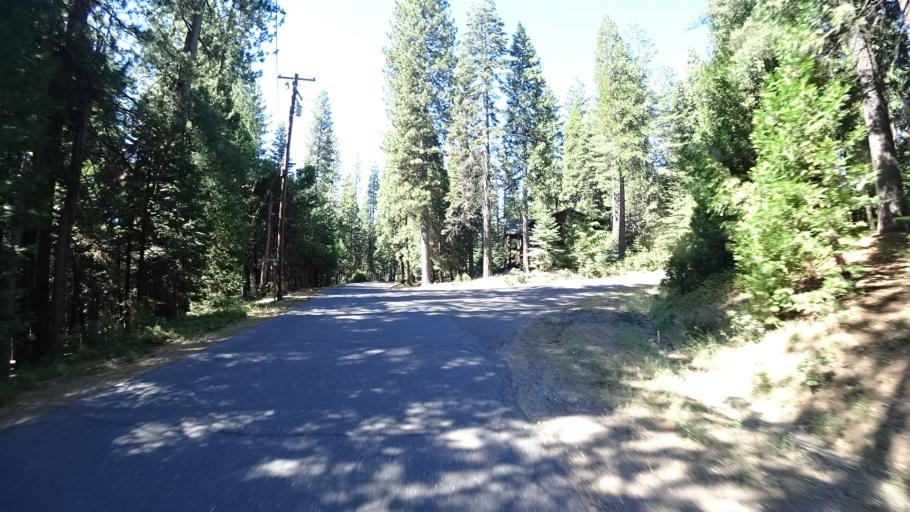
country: US
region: California
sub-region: Calaveras County
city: Arnold
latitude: 38.2814
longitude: -120.2775
